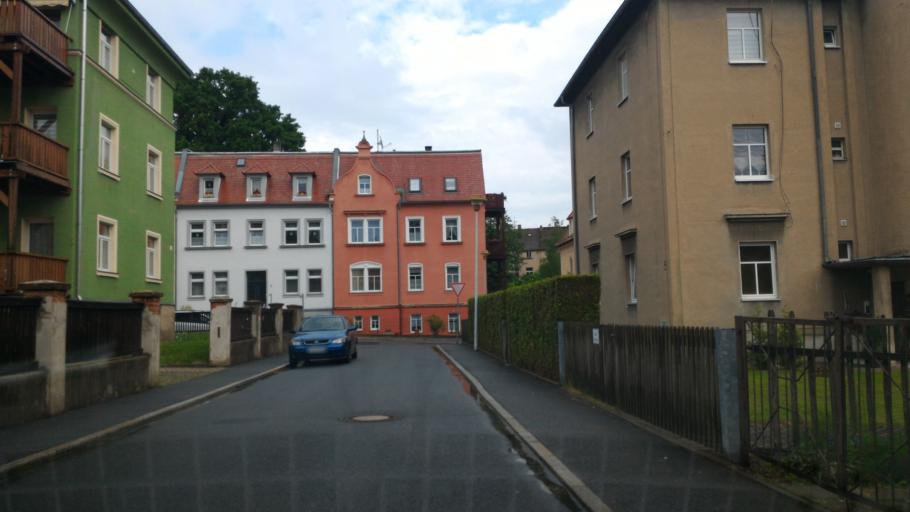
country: DE
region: Saxony
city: Zittau
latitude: 50.8984
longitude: 14.7874
